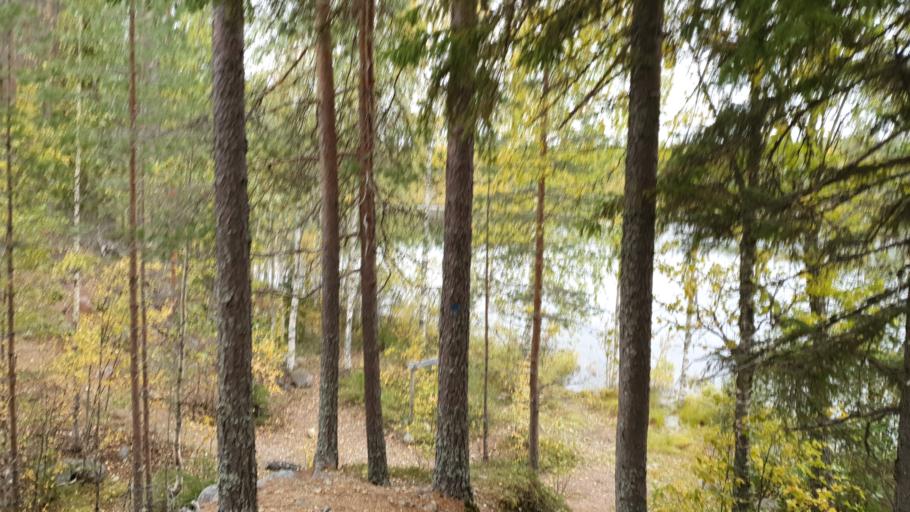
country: FI
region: Kainuu
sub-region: Kehys-Kainuu
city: Kuhmo
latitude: 64.2928
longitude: 29.3524
